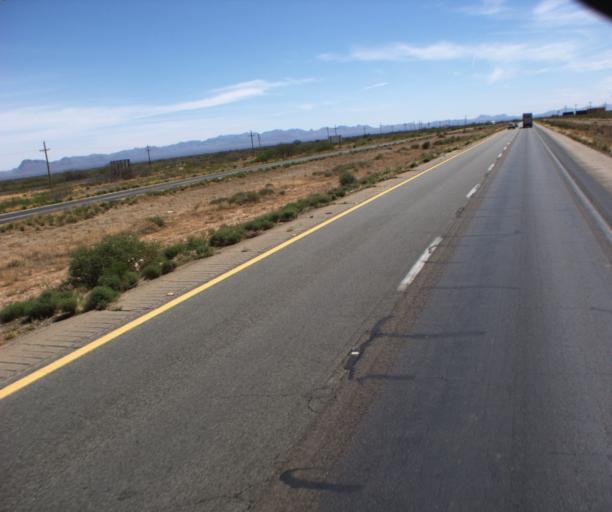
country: US
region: Arizona
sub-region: Cochise County
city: Willcox
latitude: 32.3165
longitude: -109.4390
